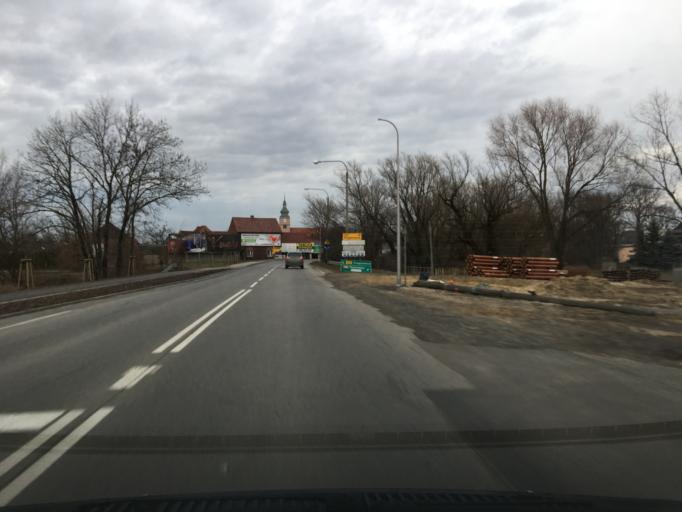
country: PL
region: Opole Voivodeship
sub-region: Powiat kedzierzynsko-kozielski
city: Kozle
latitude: 50.3434
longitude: 18.1657
